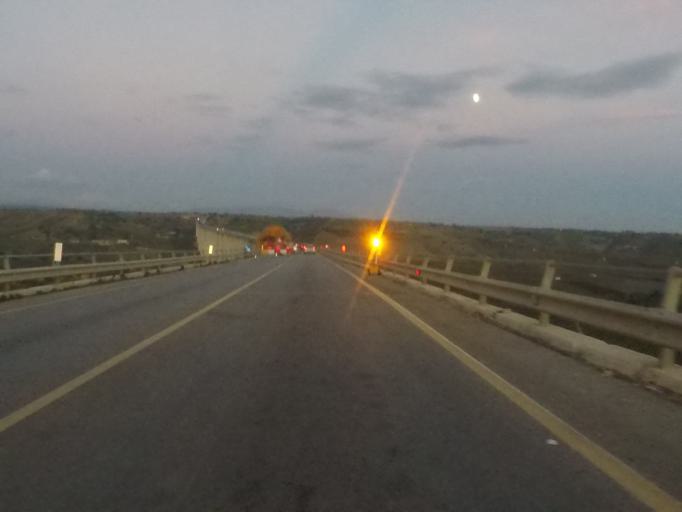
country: IT
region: Sicily
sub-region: Trapani
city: Marinella
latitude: 37.6327
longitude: 12.8791
